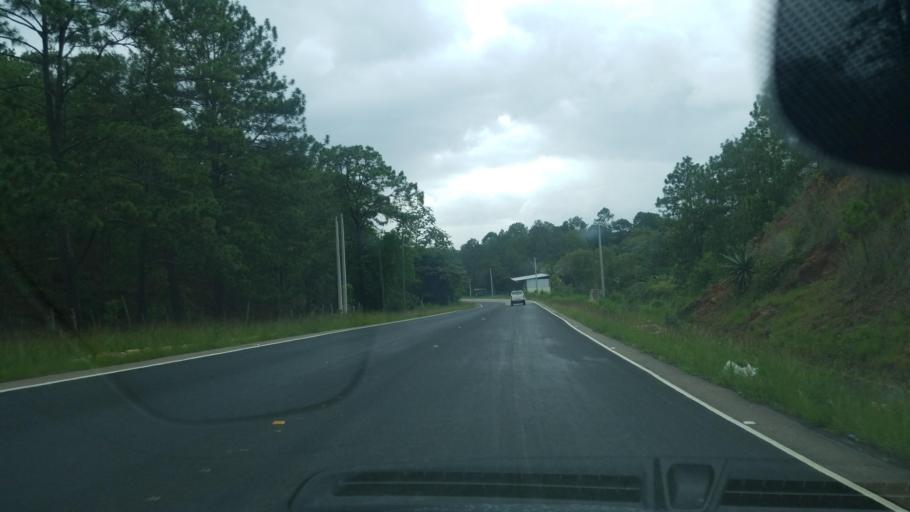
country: HN
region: Ocotepeque
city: Sinuapa
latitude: 14.4563
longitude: -89.1510
